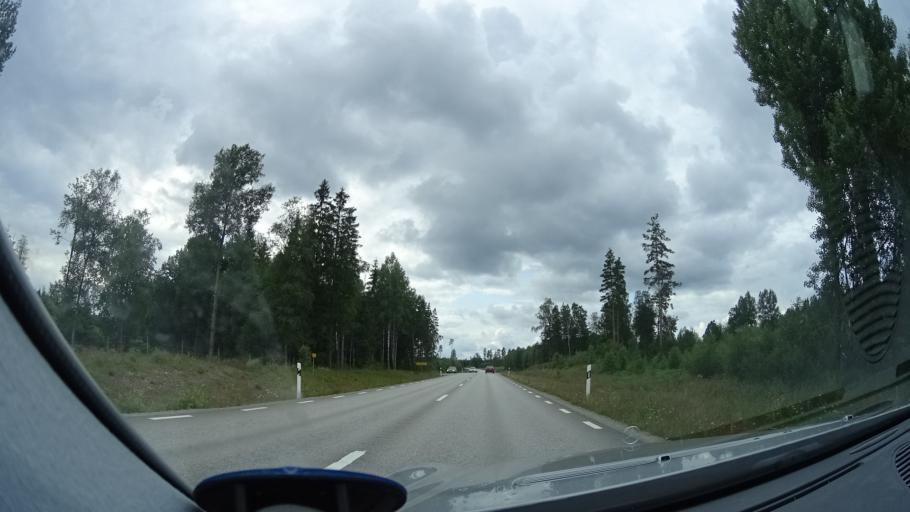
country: SE
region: Kronoberg
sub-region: Tingsryds Kommun
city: Tingsryd
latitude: 56.5066
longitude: 15.0283
